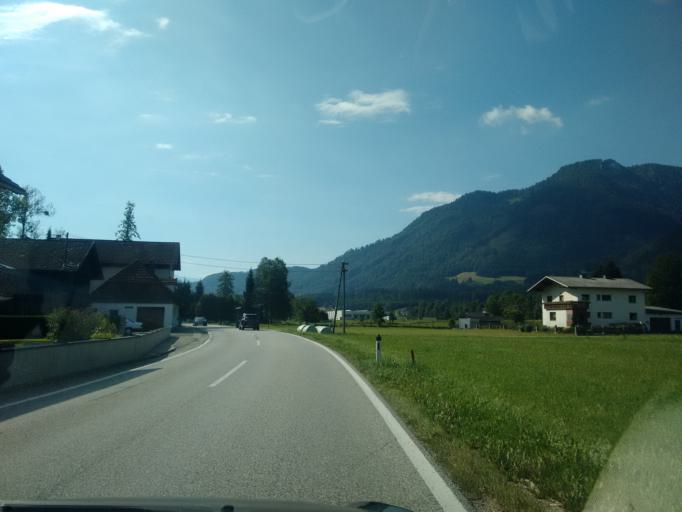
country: AT
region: Upper Austria
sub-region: Politischer Bezirk Gmunden
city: Scharnstein
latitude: 47.8819
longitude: 13.9401
